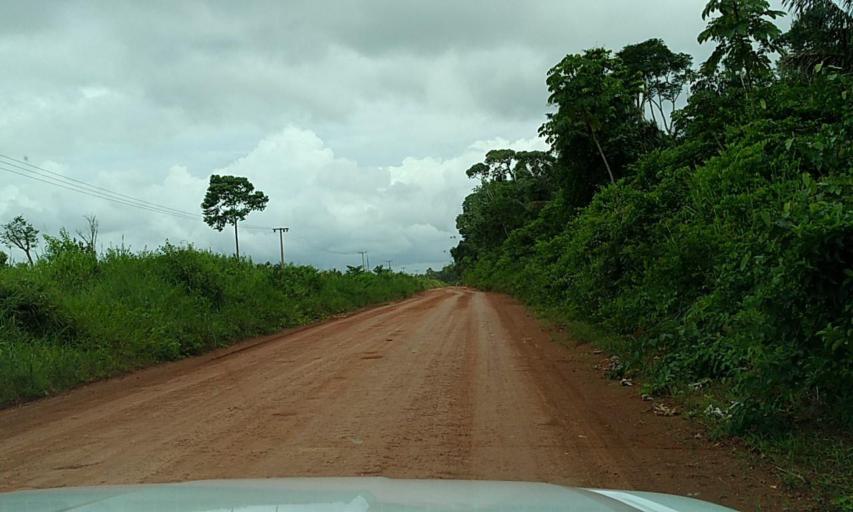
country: BR
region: Para
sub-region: Senador Jose Porfirio
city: Senador Jose Porfirio
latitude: -2.6654
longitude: -51.8403
